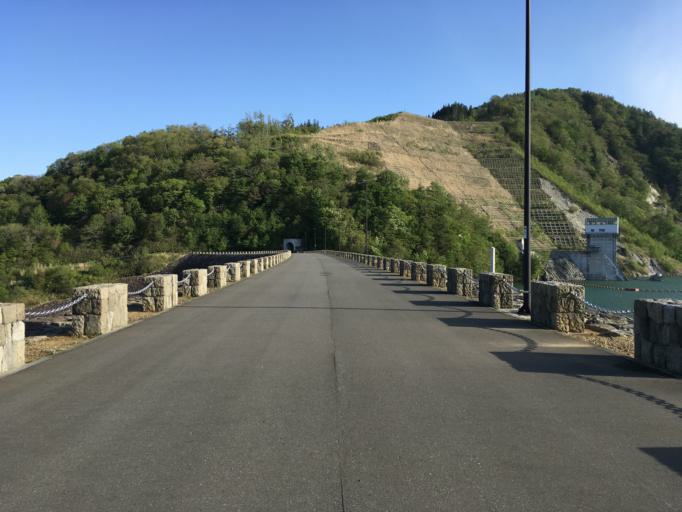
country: JP
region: Iwate
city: Mizusawa
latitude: 39.1205
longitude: 140.9199
